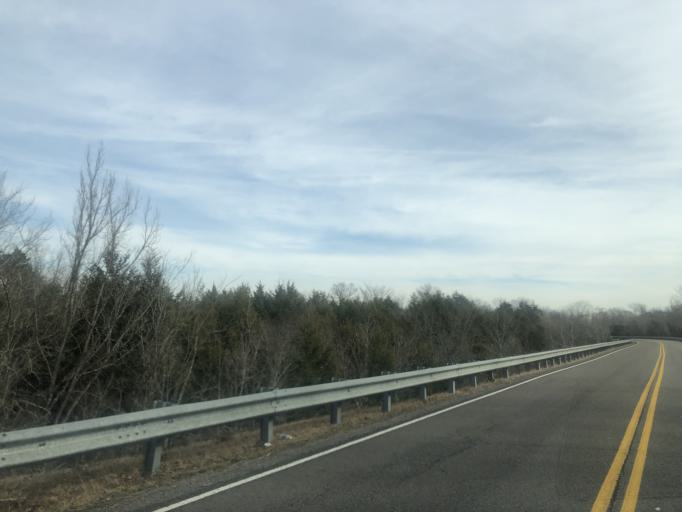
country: US
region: Tennessee
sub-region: Williamson County
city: Nolensville
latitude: 35.8577
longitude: -86.5755
